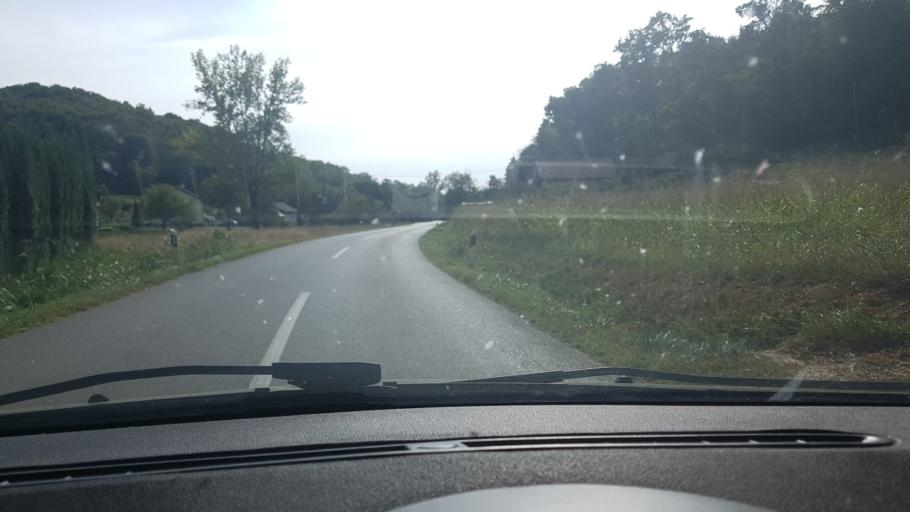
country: HR
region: Krapinsko-Zagorska
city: Zlatar
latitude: 46.1159
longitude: 16.0946
